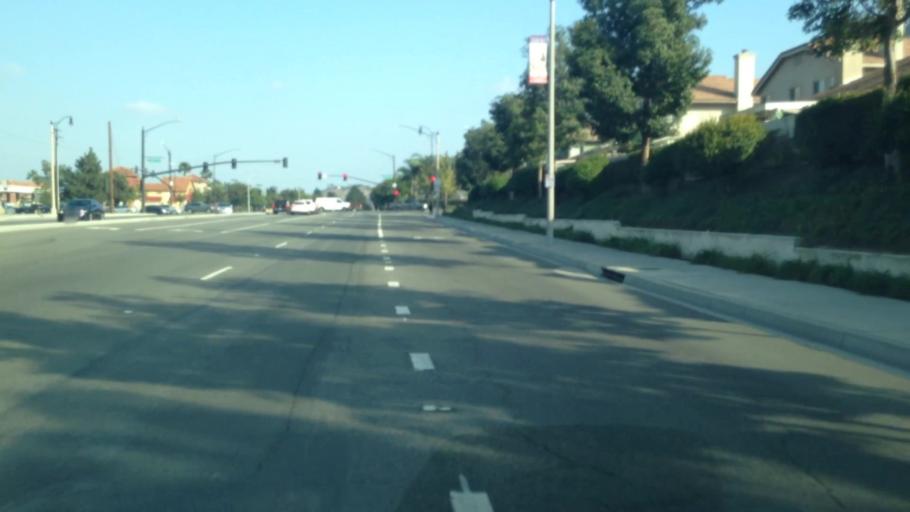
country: US
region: California
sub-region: Riverside County
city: Sunnyslope
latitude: 34.0482
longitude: -117.4371
